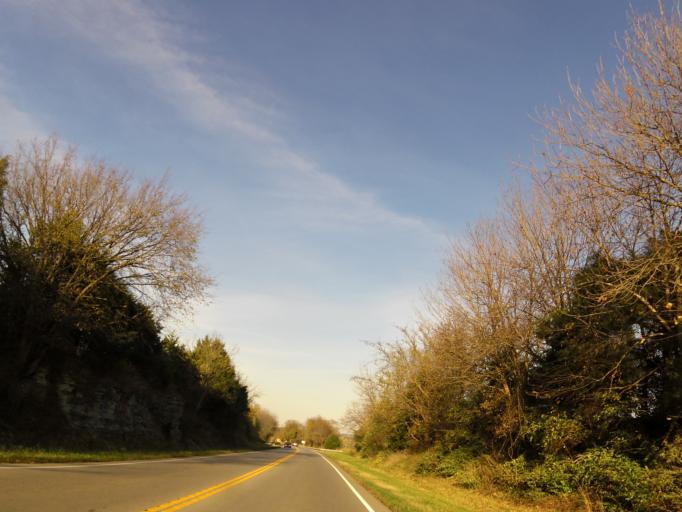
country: US
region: Kentucky
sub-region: Lincoln County
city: Stanford
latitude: 37.5574
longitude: -84.6301
